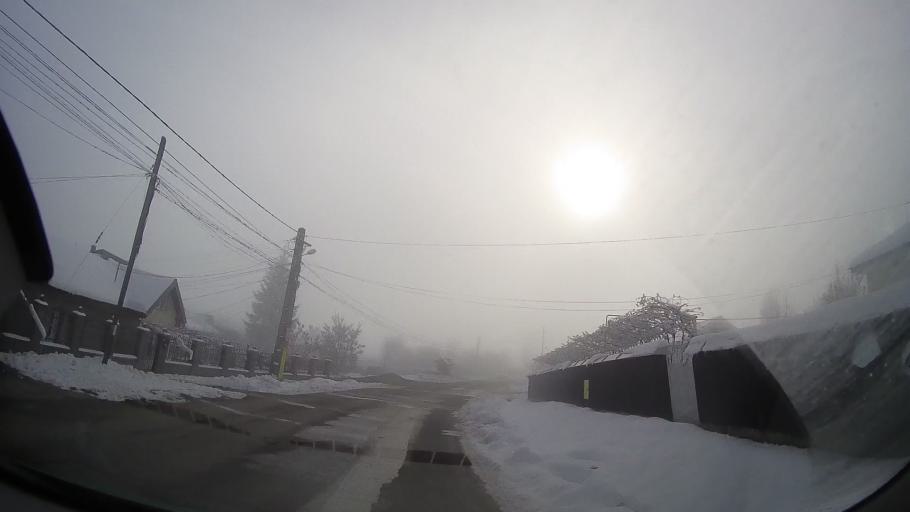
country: RO
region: Iasi
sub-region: Comuna Valea Seaca
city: Topile
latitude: 47.2450
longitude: 26.6649
